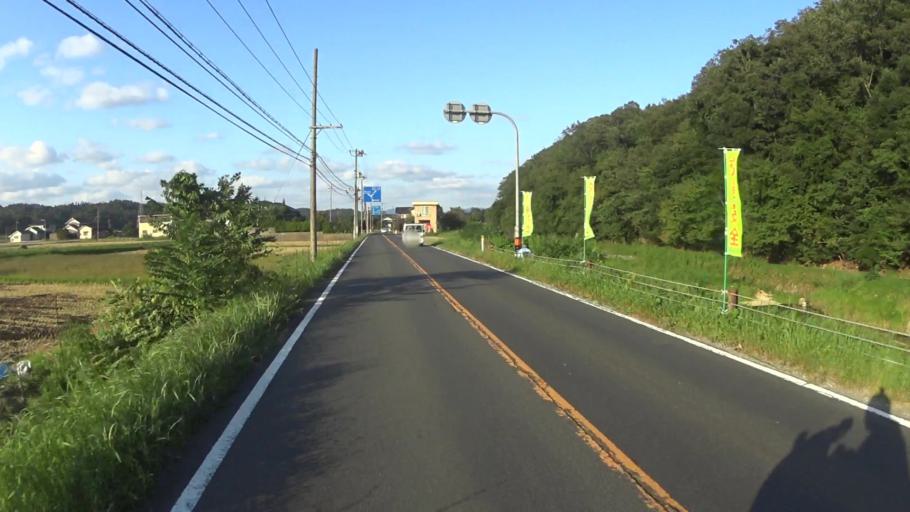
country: JP
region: Kyoto
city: Miyazu
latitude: 35.5968
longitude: 135.0444
